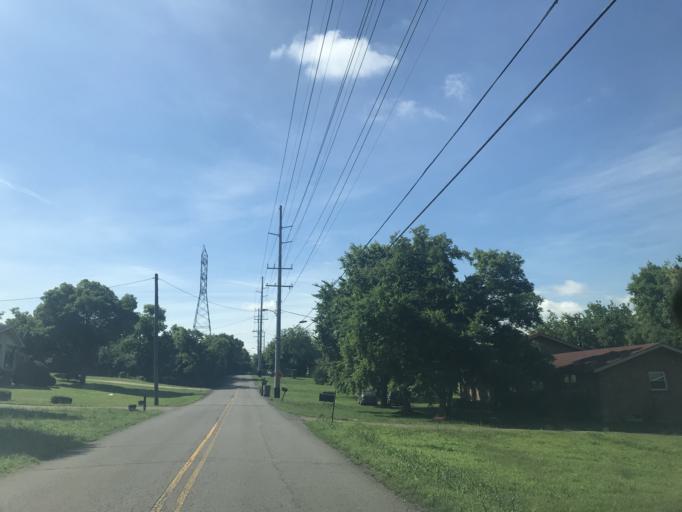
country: US
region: Tennessee
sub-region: Davidson County
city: Nashville
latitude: 36.1955
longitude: -86.8419
